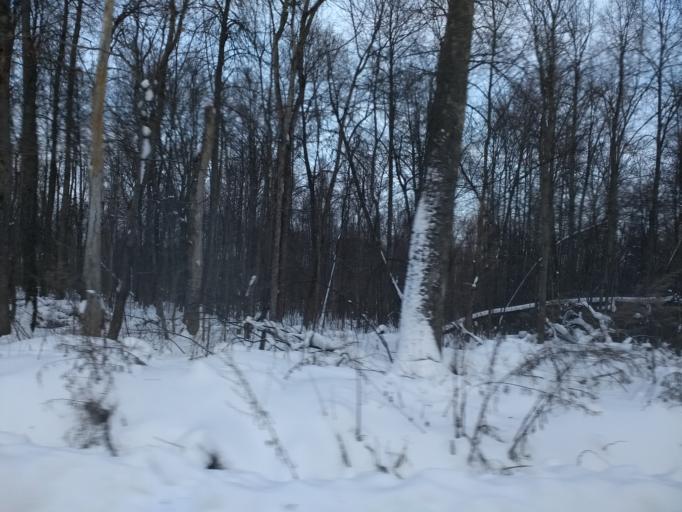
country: RU
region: Bashkortostan
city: Kudeyevskiy
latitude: 54.7145
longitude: 56.6353
